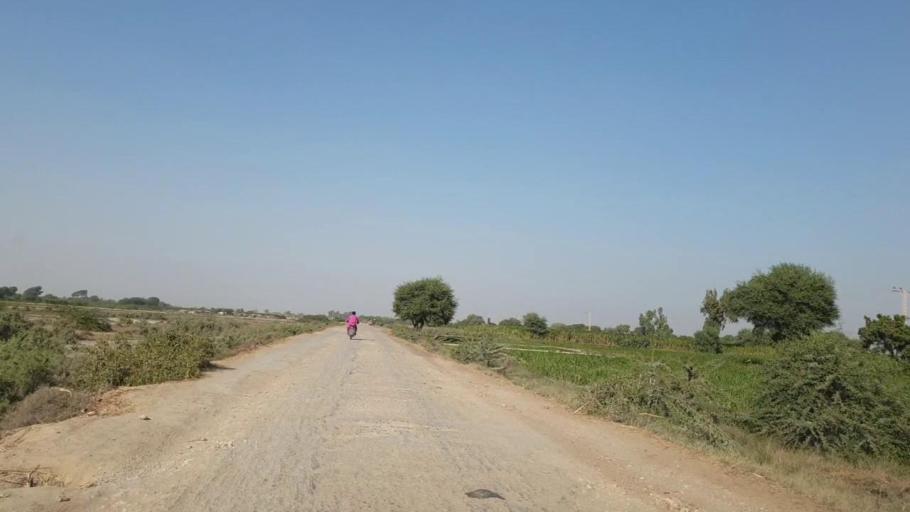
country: PK
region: Sindh
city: Digri
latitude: 25.0405
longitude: 69.1047
